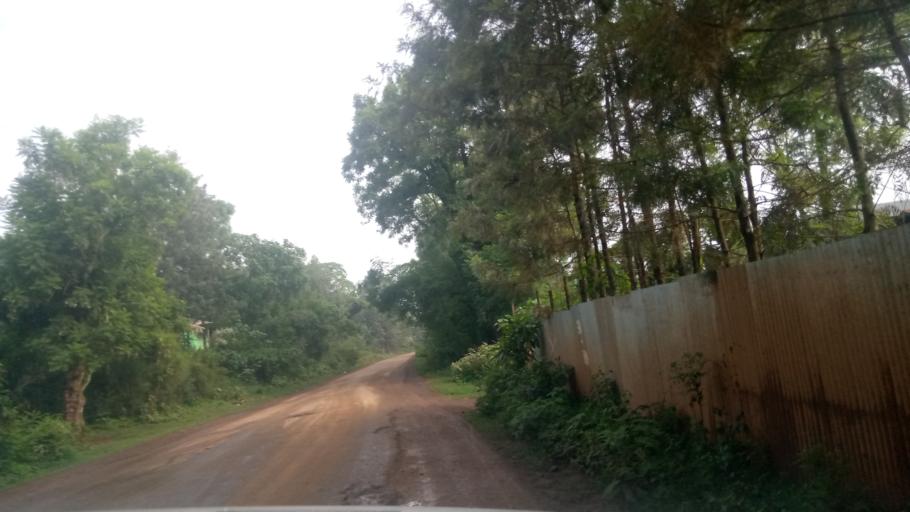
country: ET
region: Oromiya
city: Agaro
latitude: 7.8425
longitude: 36.6607
